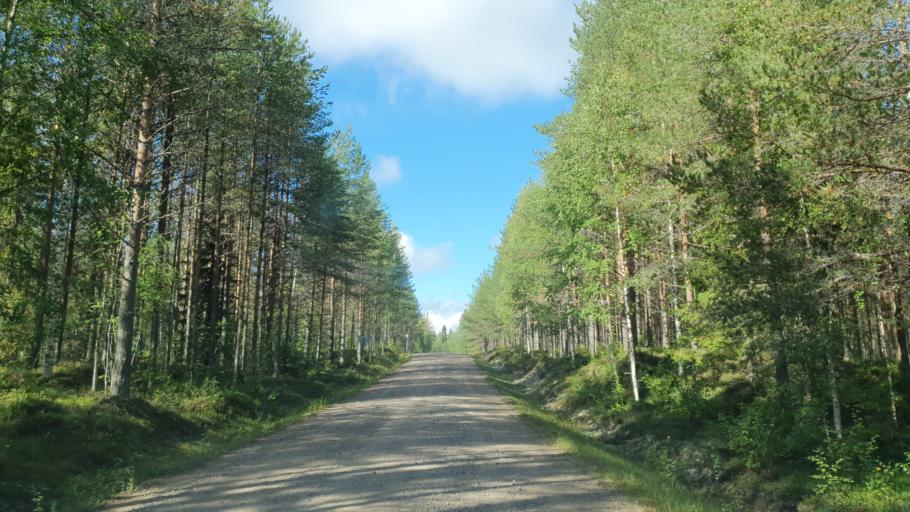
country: FI
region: Kainuu
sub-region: Kehys-Kainuu
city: Kuhmo
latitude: 64.0332
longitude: 29.1703
